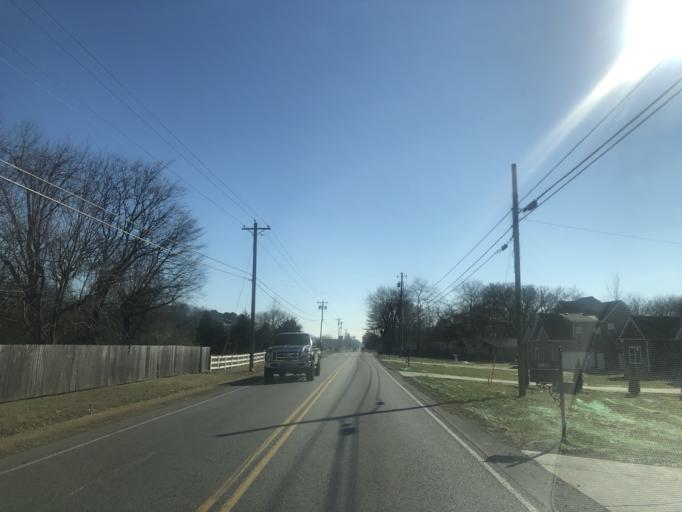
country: US
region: Tennessee
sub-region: Rutherford County
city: Smyrna
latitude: 35.9357
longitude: -86.4944
